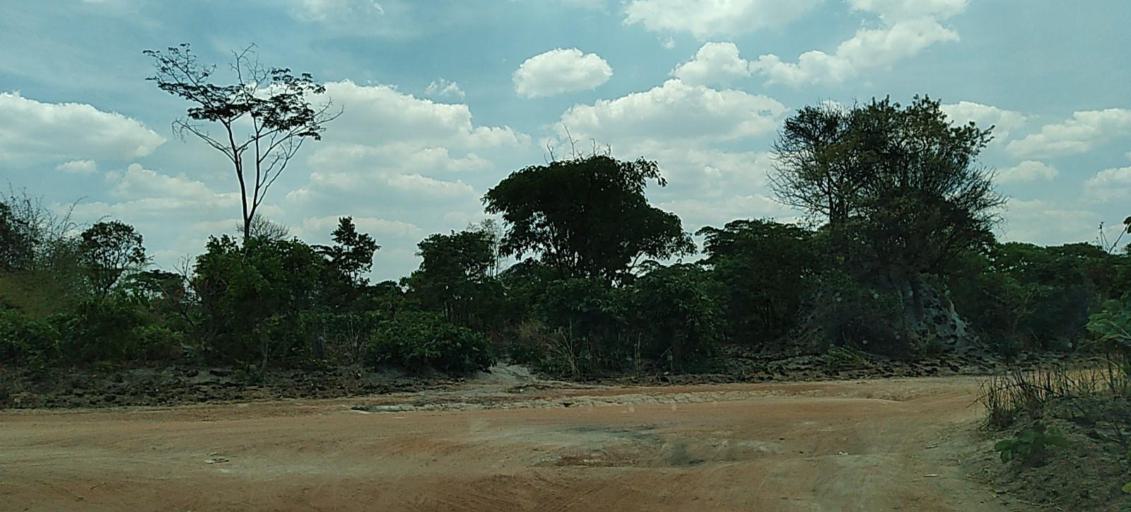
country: ZM
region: Copperbelt
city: Chililabombwe
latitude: -12.3888
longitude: 27.9175
